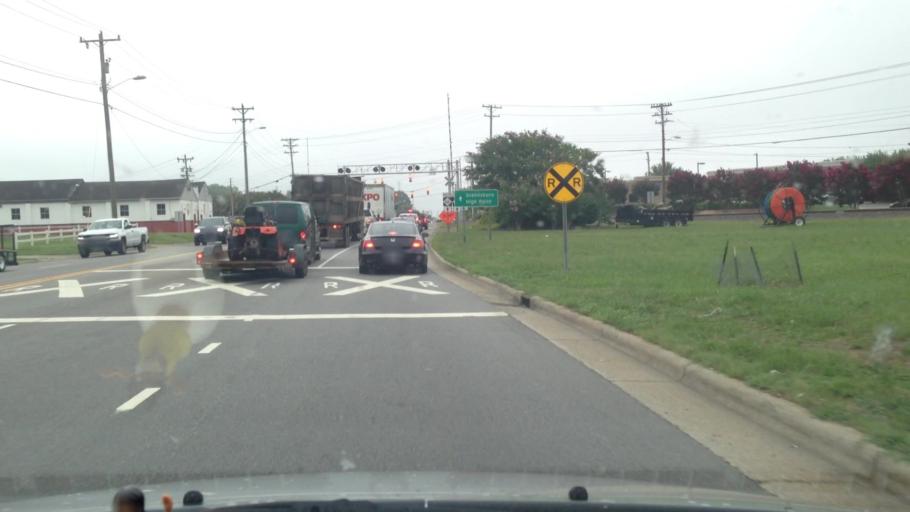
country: US
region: North Carolina
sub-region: Forsyth County
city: Kernersville
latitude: 36.1176
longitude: -80.0667
